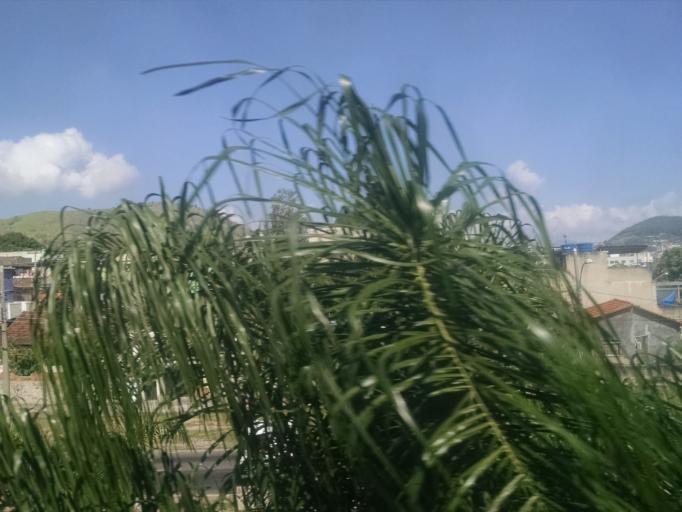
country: BR
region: Rio de Janeiro
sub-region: Duque De Caxias
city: Duque de Caxias
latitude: -22.8500
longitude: -43.3200
